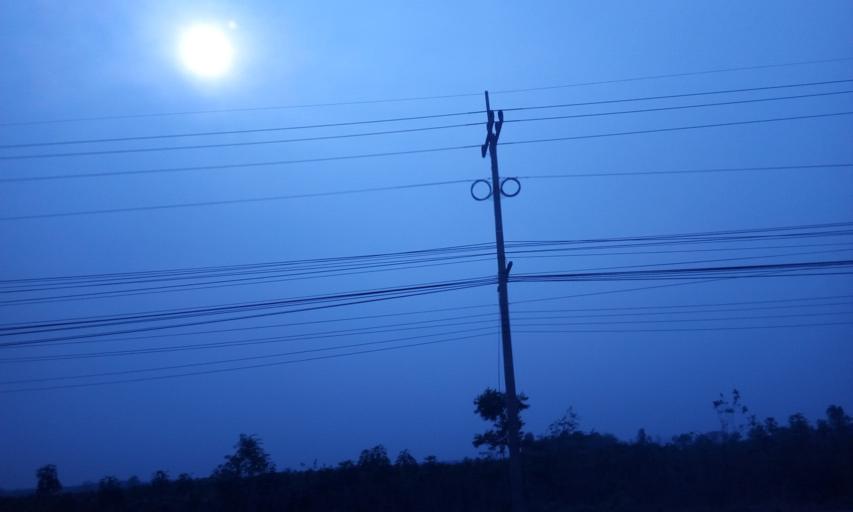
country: TH
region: Chachoengsao
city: Plaeng Yao
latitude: 13.5469
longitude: 101.2632
